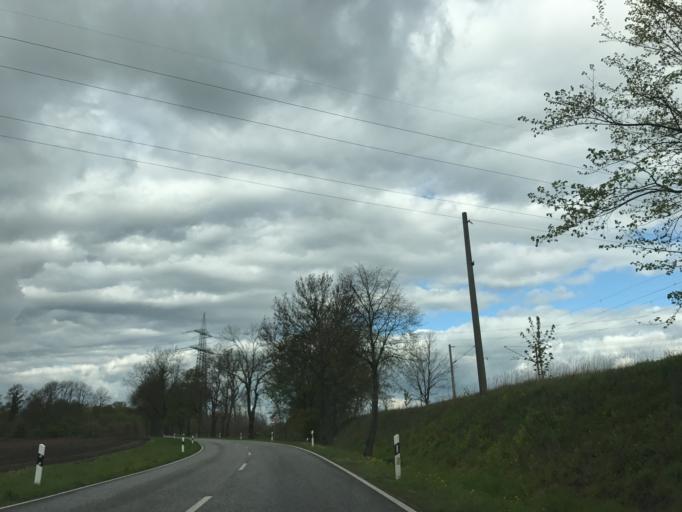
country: DE
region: Brandenburg
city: Brieselang
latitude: 52.5937
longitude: 12.9577
